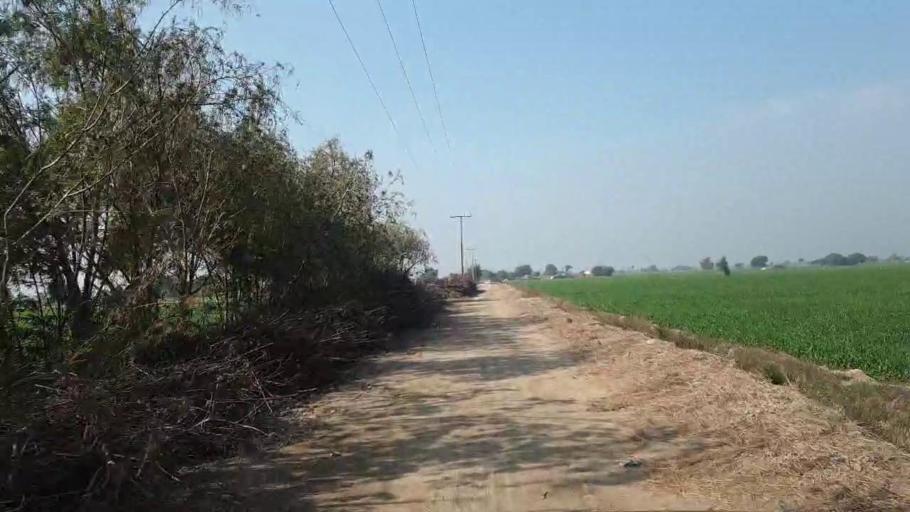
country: PK
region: Sindh
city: Shahdadpur
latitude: 26.0208
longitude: 68.5739
